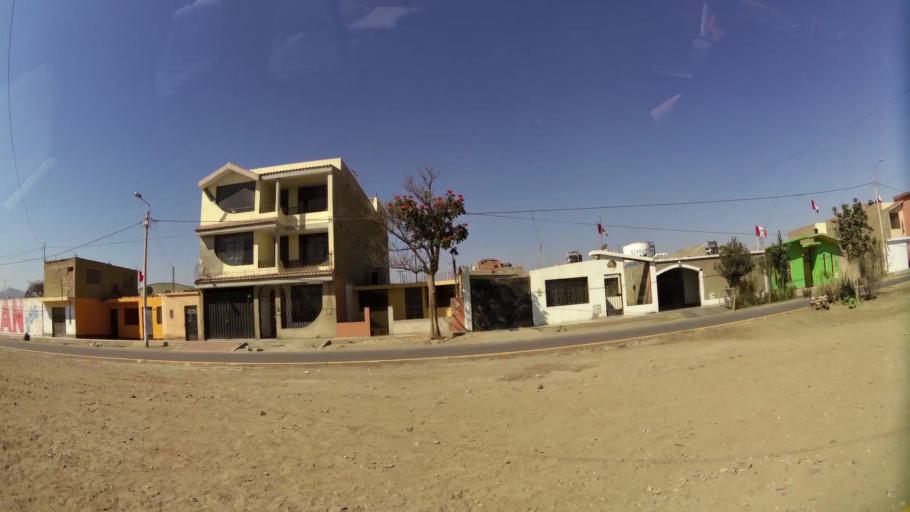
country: PE
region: Ica
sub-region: Provincia de Ica
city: La Tinguina
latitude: -14.0376
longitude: -75.7010
